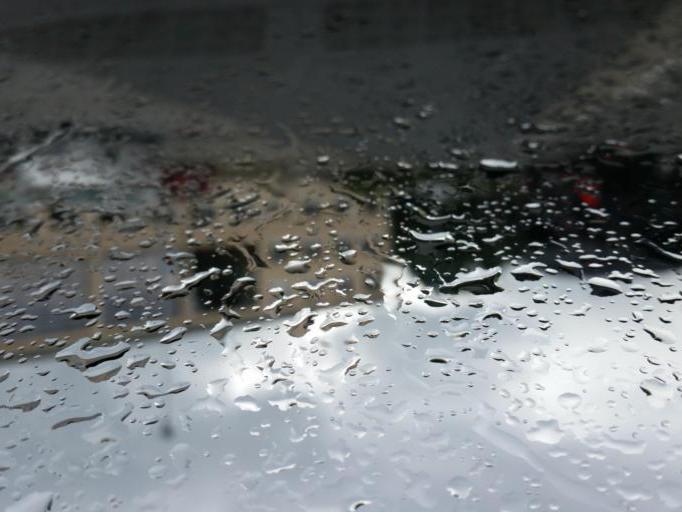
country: DE
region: Saxony
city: Bautzen
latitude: 51.1857
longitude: 14.4245
